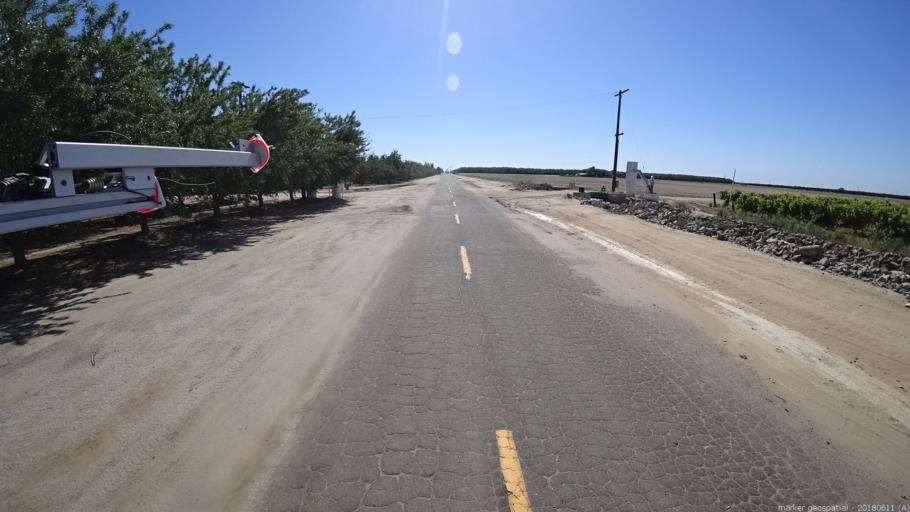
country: US
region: California
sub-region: Madera County
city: Madera
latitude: 36.9456
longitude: -120.1424
